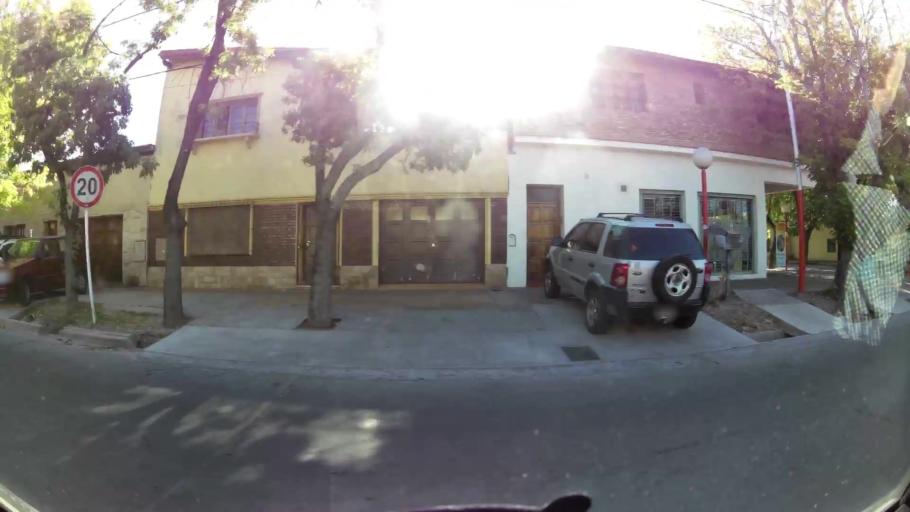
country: AR
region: Mendoza
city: Mendoza
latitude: -32.9011
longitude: -68.8245
